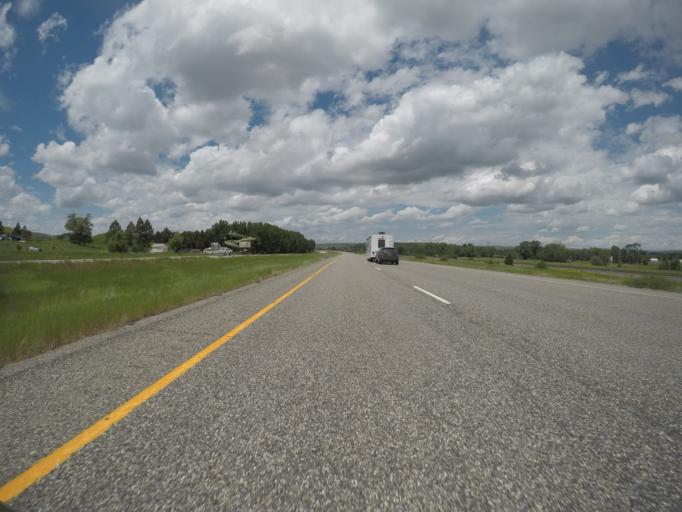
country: US
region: Montana
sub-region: Sweet Grass County
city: Big Timber
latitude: 45.7722
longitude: -109.7961
